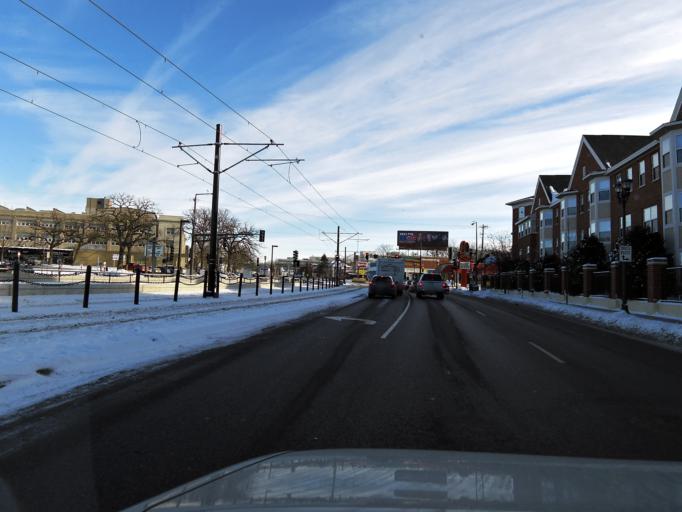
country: US
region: Minnesota
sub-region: Ramsey County
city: Falcon Heights
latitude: 44.9560
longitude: -93.1781
